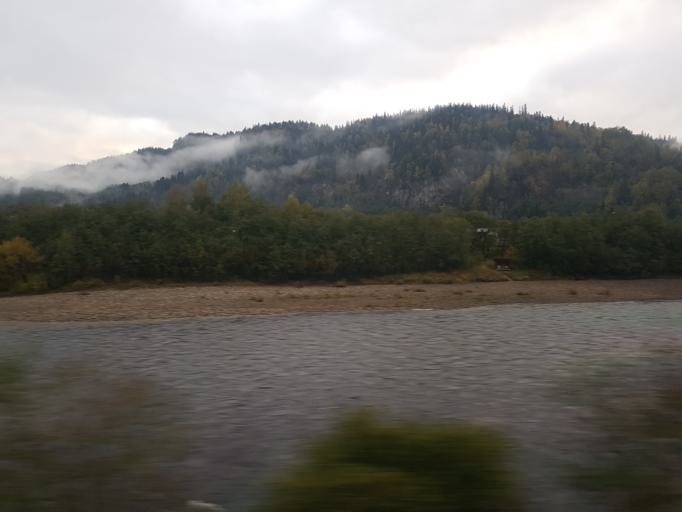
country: NO
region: Sor-Trondelag
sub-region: Melhus
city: Lundamo
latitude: 63.0976
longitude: 10.2371
